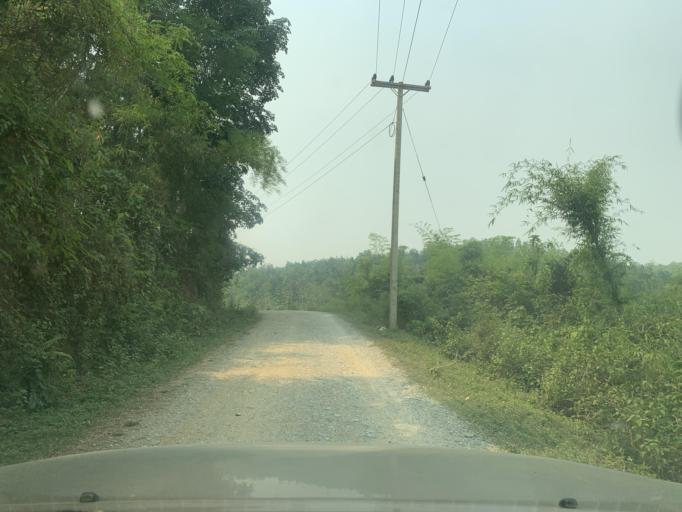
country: LA
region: Louangphabang
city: Louangphabang
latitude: 19.8893
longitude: 102.2517
